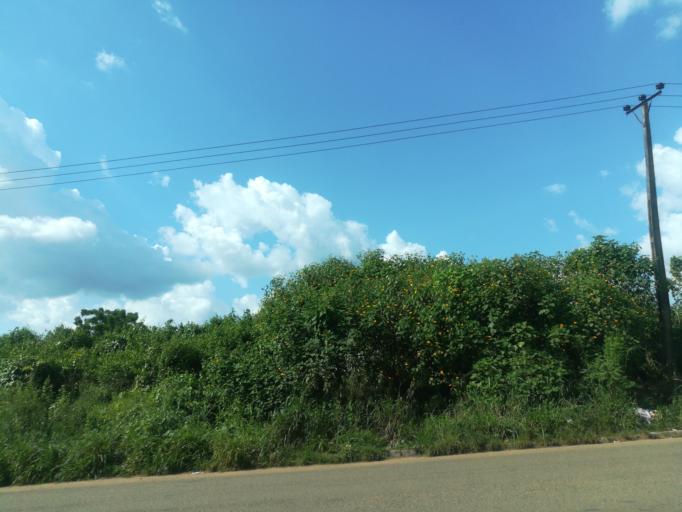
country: NG
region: Oyo
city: Egbeda
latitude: 7.4251
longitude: 3.9887
